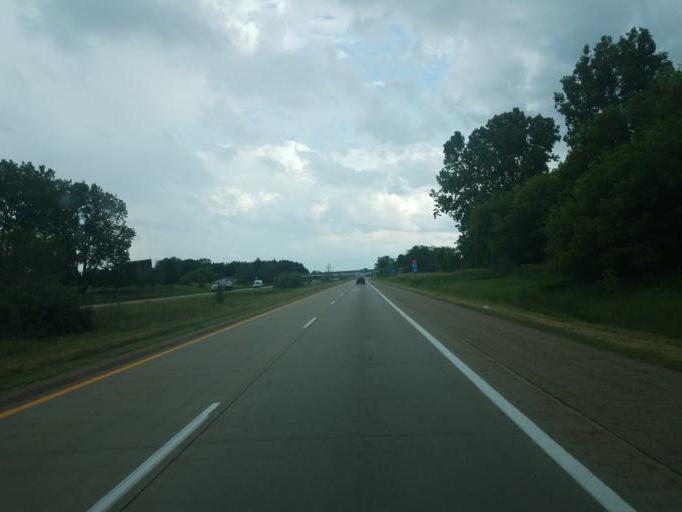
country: US
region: Michigan
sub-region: Calhoun County
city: Marshall
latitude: 42.2797
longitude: -84.9950
